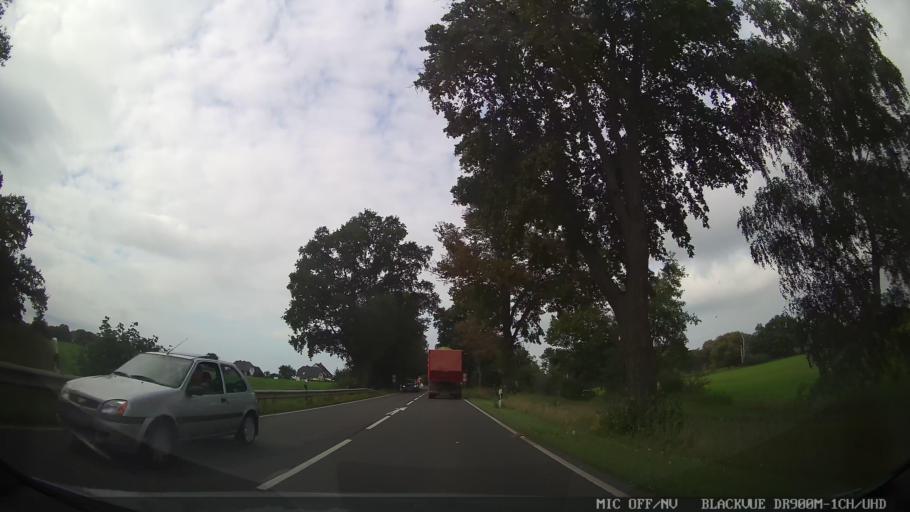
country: DE
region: Lower Saxony
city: Klein Schwulper
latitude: 52.3218
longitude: 10.4466
